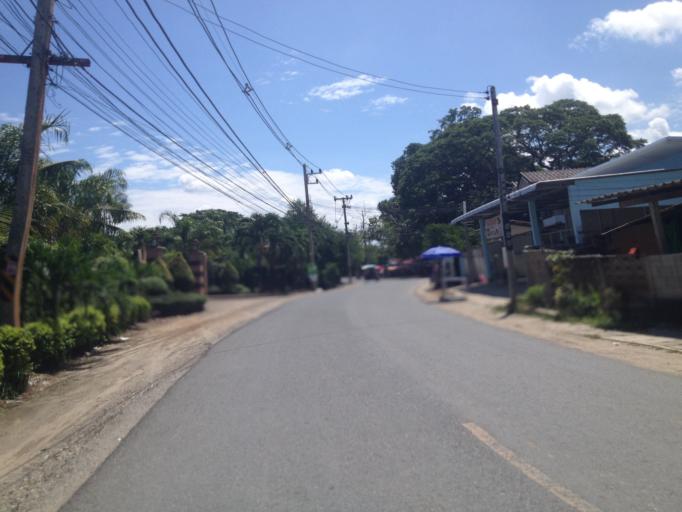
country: TH
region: Chiang Mai
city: Hang Dong
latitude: 18.6718
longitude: 98.9242
